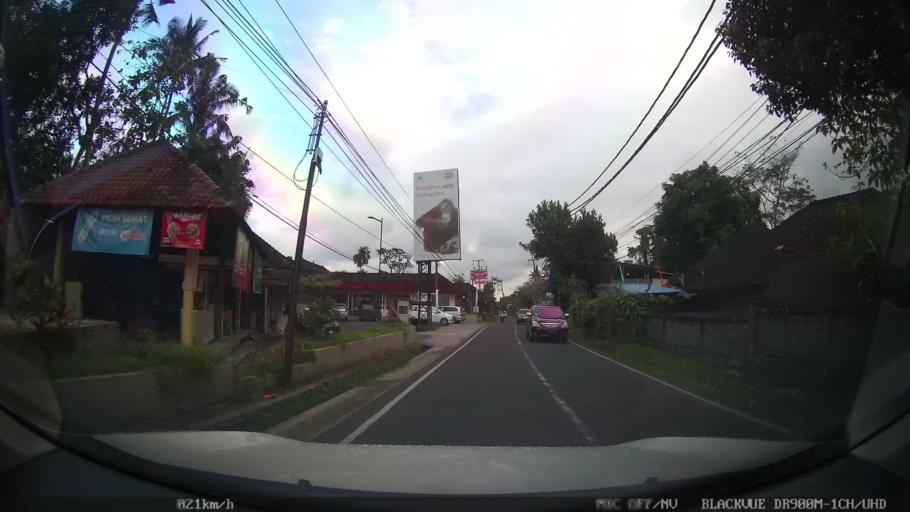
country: ID
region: Bali
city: Pegongan
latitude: -8.4897
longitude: 115.2464
